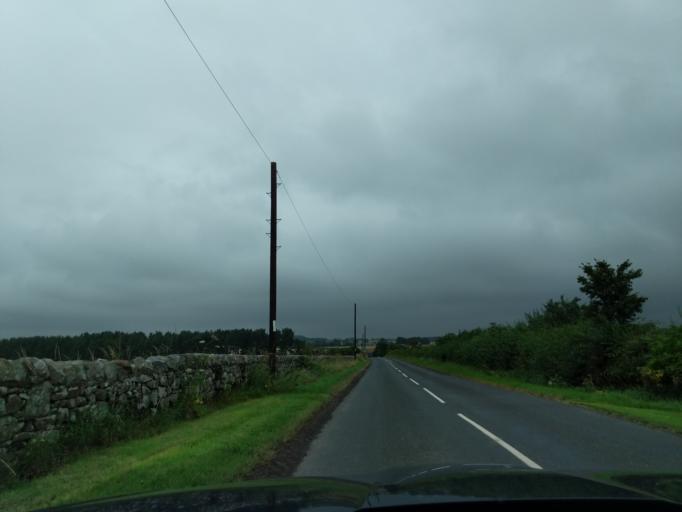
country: GB
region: England
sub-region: Northumberland
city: Ford
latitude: 55.6608
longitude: -2.1065
